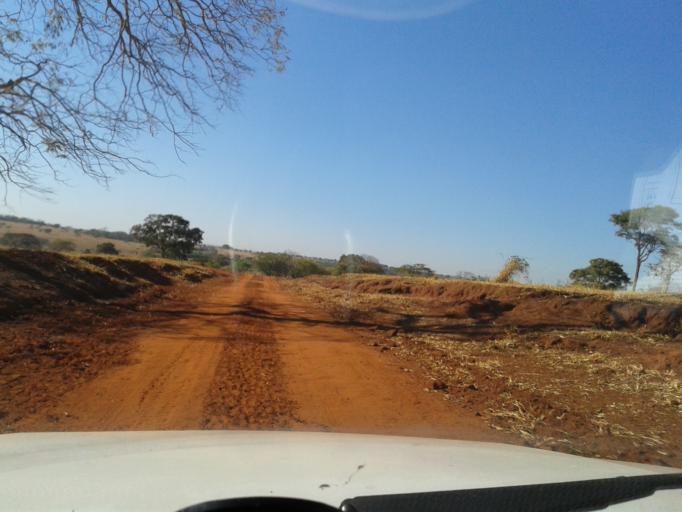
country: BR
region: Minas Gerais
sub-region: Santa Vitoria
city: Santa Vitoria
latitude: -19.0562
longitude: -49.9295
